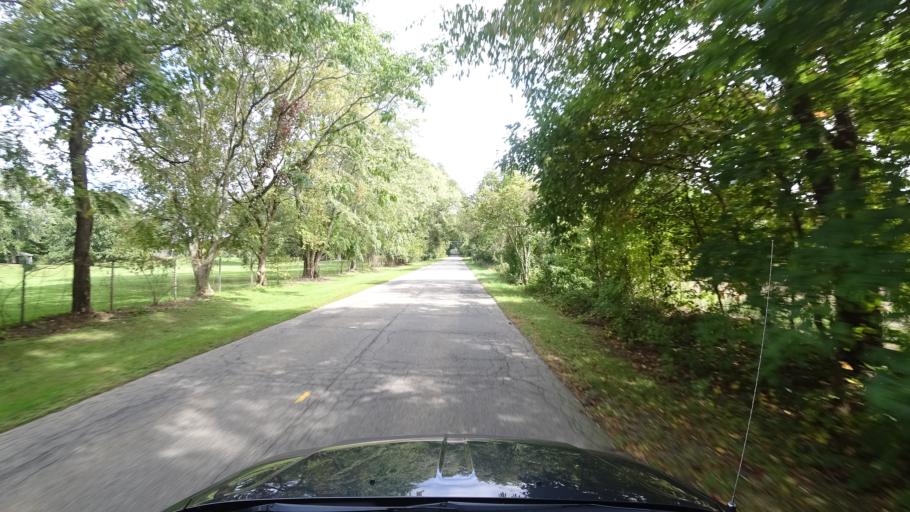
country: US
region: Indiana
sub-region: LaPorte County
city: Trail Creek
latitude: 41.7092
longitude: -86.8499
